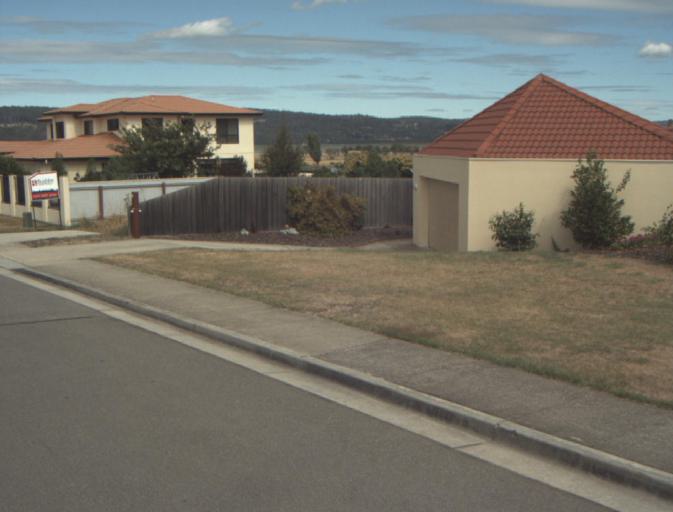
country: AU
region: Tasmania
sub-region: Launceston
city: Mayfield
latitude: -41.3874
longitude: 147.1099
